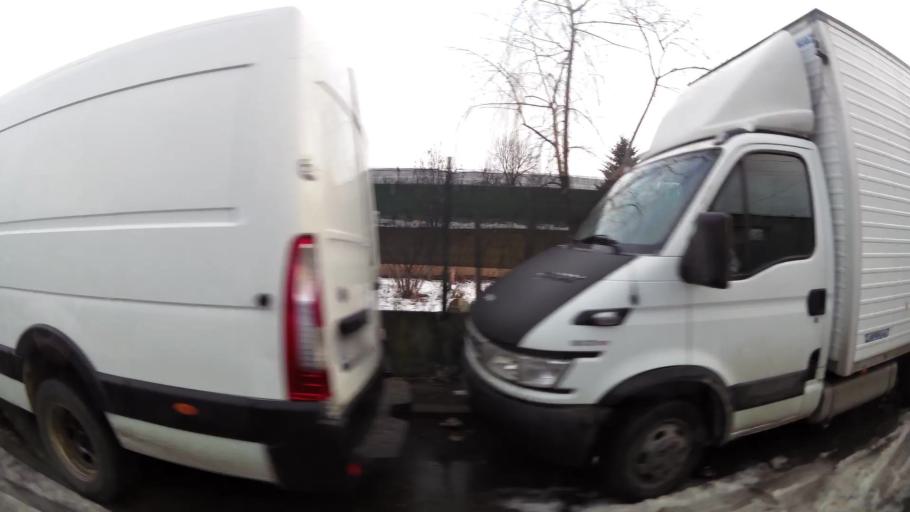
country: RO
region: Ilfov
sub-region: Comuna Fundeni-Dobroesti
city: Fundeni
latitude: 44.4710
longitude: 26.1663
